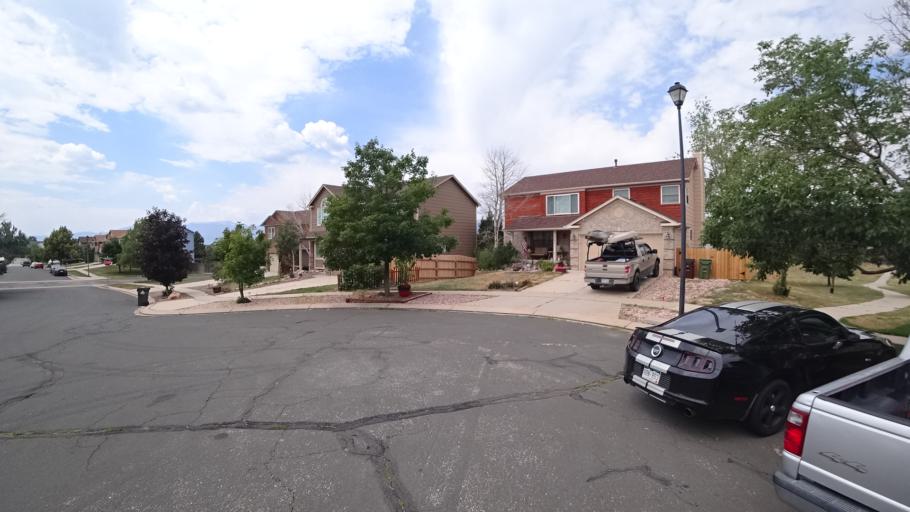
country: US
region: Colorado
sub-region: El Paso County
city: Black Forest
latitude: 38.9610
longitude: -104.7740
